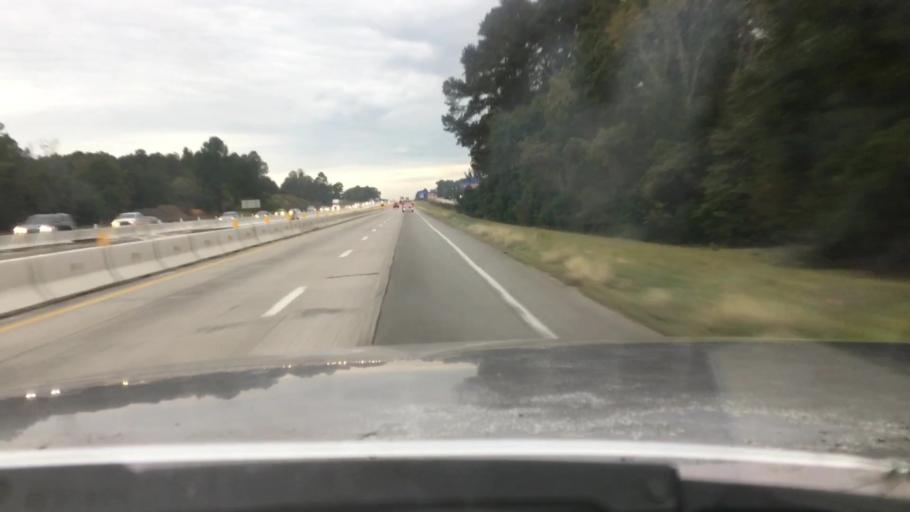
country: US
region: South Carolina
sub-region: Lexington County
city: Lexington
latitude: 33.9650
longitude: -81.2120
